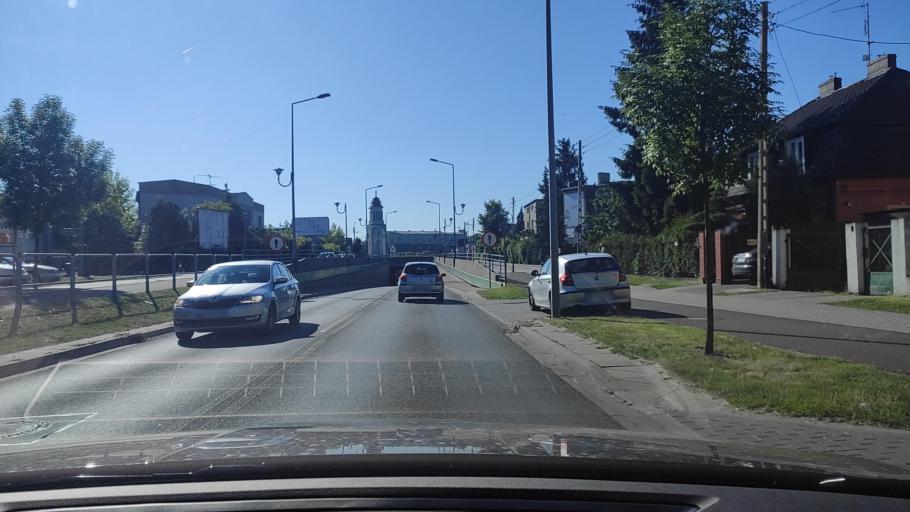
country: PL
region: Greater Poland Voivodeship
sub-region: Powiat poznanski
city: Lubon
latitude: 52.3710
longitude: 16.8984
